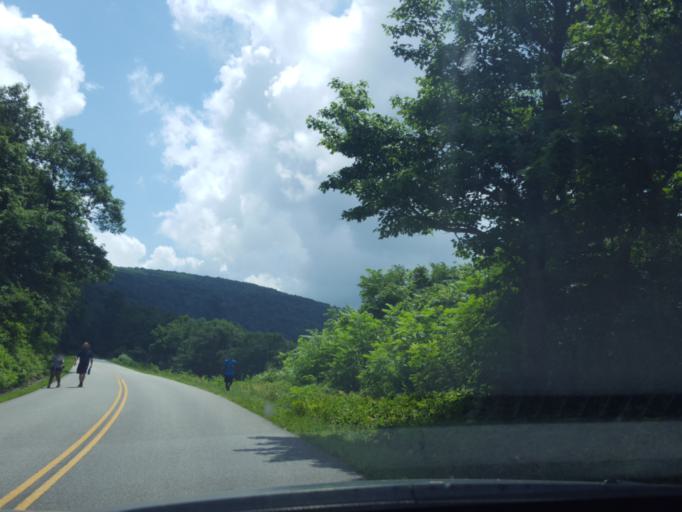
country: US
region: Virginia
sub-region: Augusta County
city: Lyndhurst
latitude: 37.9597
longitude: -78.9120
